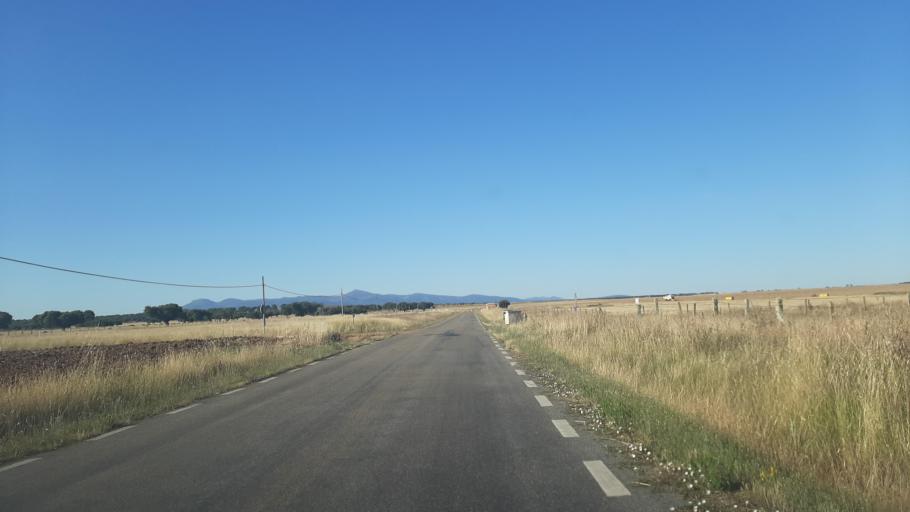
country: ES
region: Castille and Leon
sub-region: Provincia de Salamanca
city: Cabrillas
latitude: 40.7189
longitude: -6.1770
